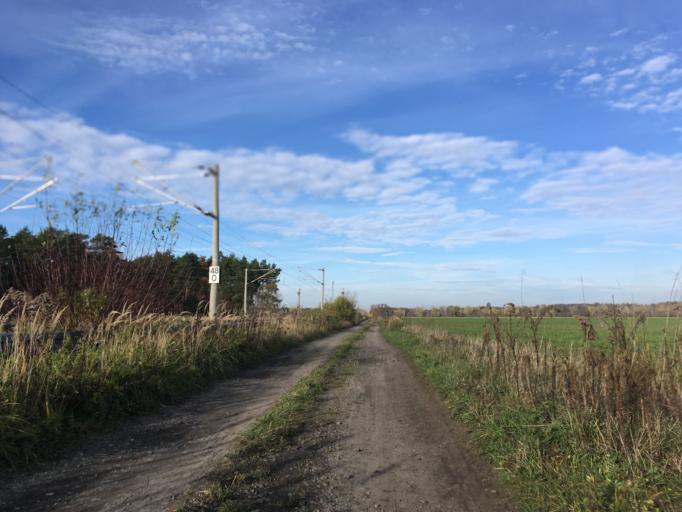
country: DE
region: Brandenburg
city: Halbe
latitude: 52.1271
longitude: 13.6823
